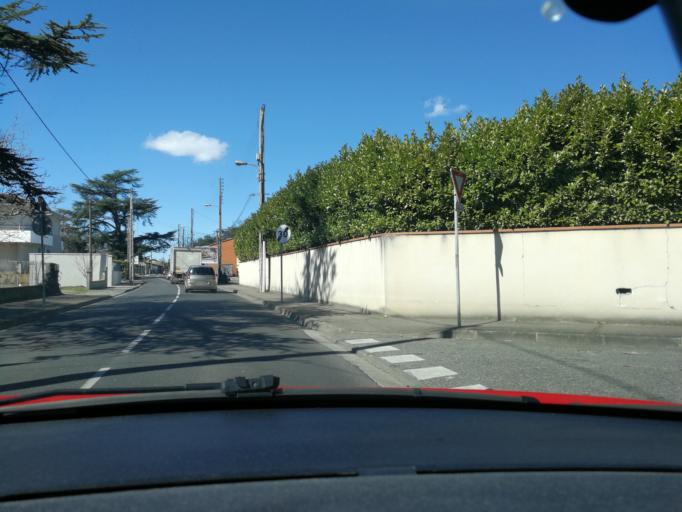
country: FR
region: Midi-Pyrenees
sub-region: Departement de la Haute-Garonne
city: Cugnaux
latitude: 43.5551
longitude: 1.3730
